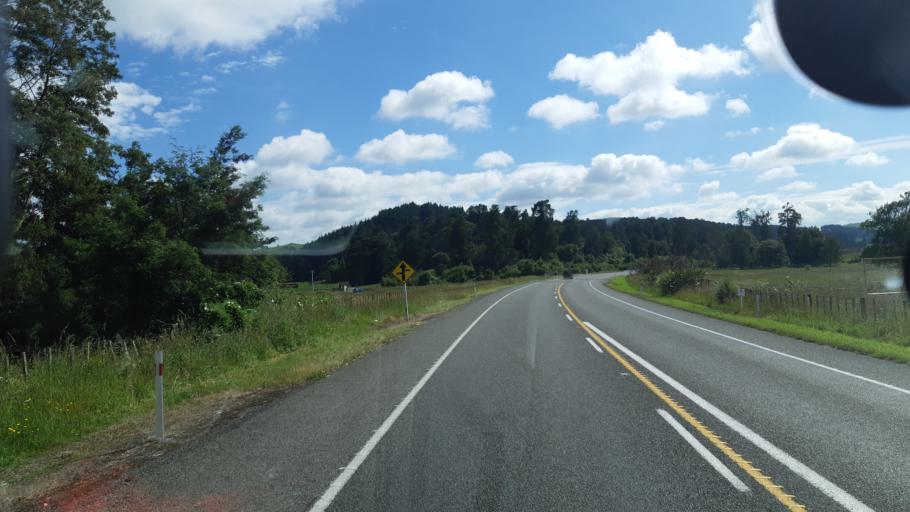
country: NZ
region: Manawatu-Wanganui
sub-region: Rangitikei District
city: Bulls
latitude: -39.9667
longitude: 175.5230
